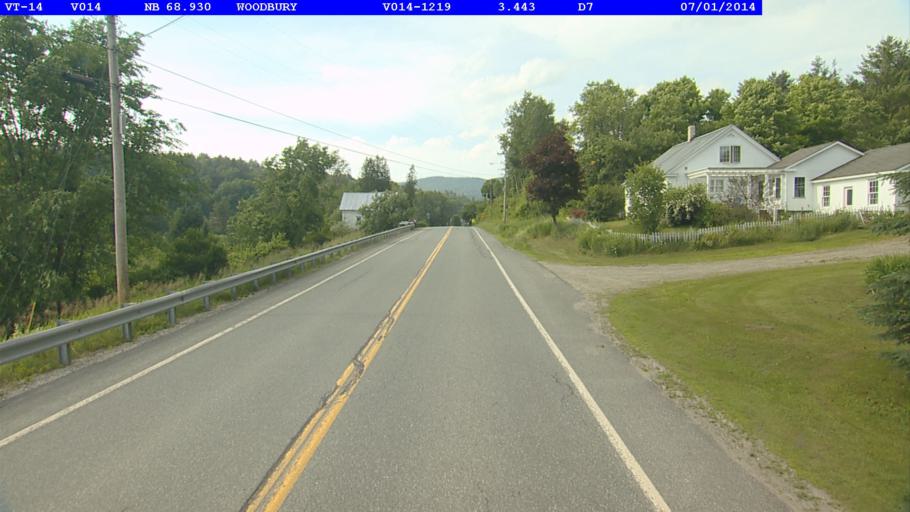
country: US
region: Vermont
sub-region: Caledonia County
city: Hardwick
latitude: 44.4378
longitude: -72.4135
